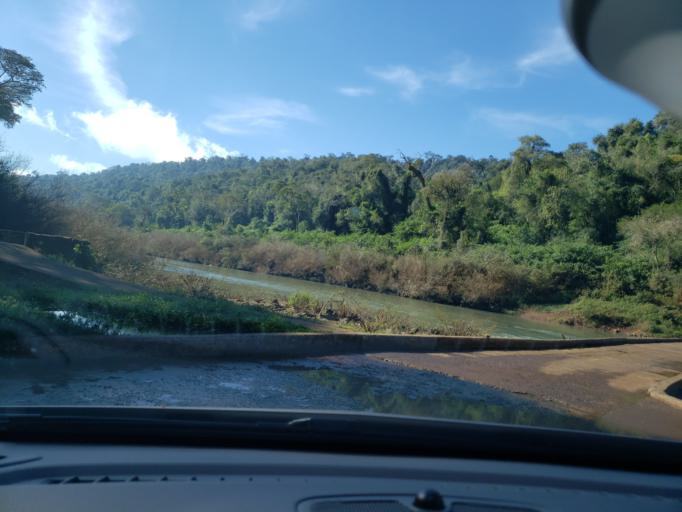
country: BR
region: Rio Grande do Sul
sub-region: Tres Passos
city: Tres Passos
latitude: -27.1448
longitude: -53.9078
